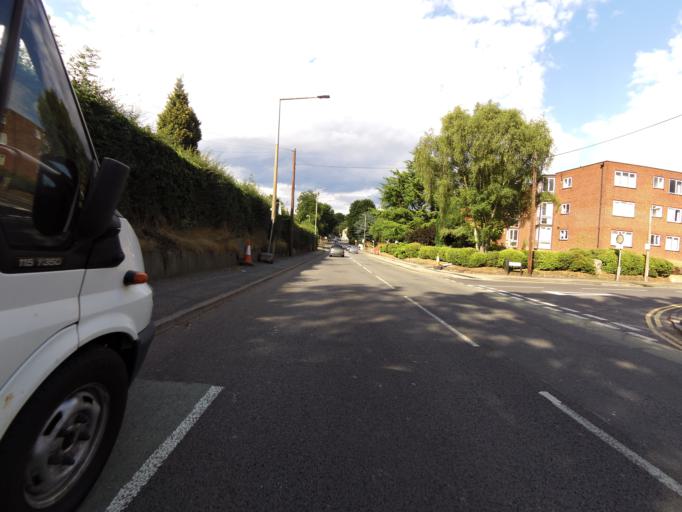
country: GB
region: England
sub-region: Hertfordshire
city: Broxbourne
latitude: 51.7508
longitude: -0.0176
